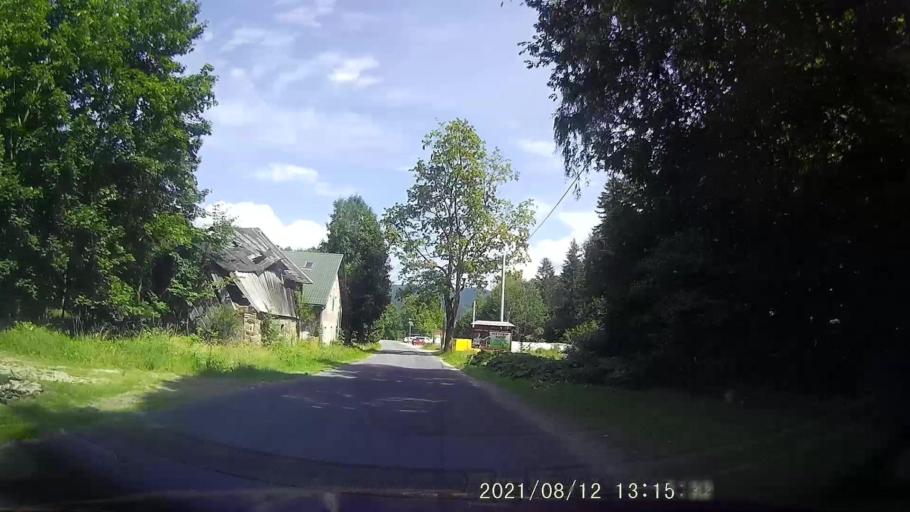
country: PL
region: Lower Silesian Voivodeship
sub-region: Powiat klodzki
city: Stronie Slaskie
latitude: 50.2615
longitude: 16.8693
